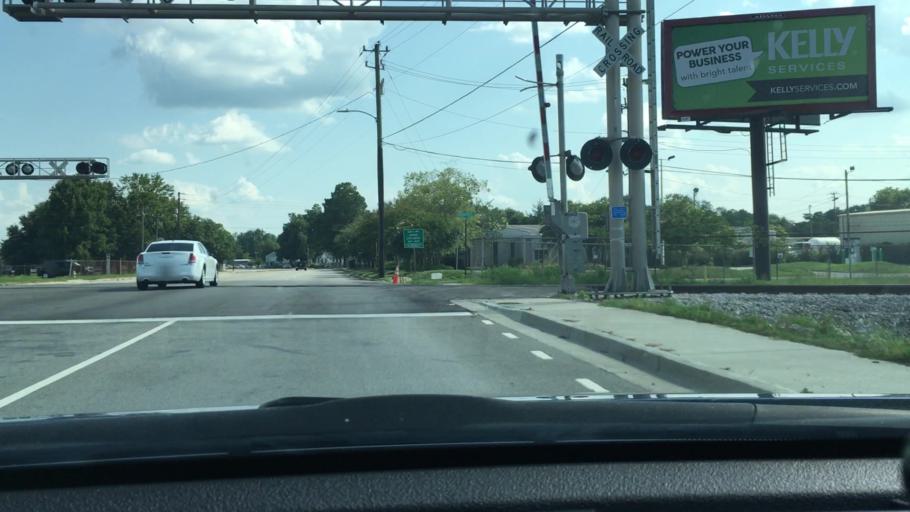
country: US
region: South Carolina
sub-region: Sumter County
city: Sumter
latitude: 33.9138
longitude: -80.3370
